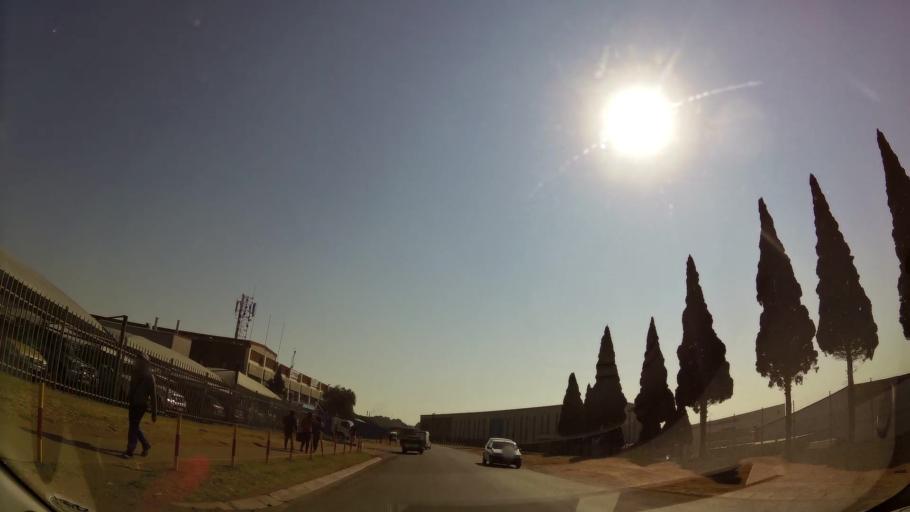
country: ZA
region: Gauteng
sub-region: Ekurhuleni Metropolitan Municipality
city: Boksburg
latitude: -26.1698
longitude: 28.2108
